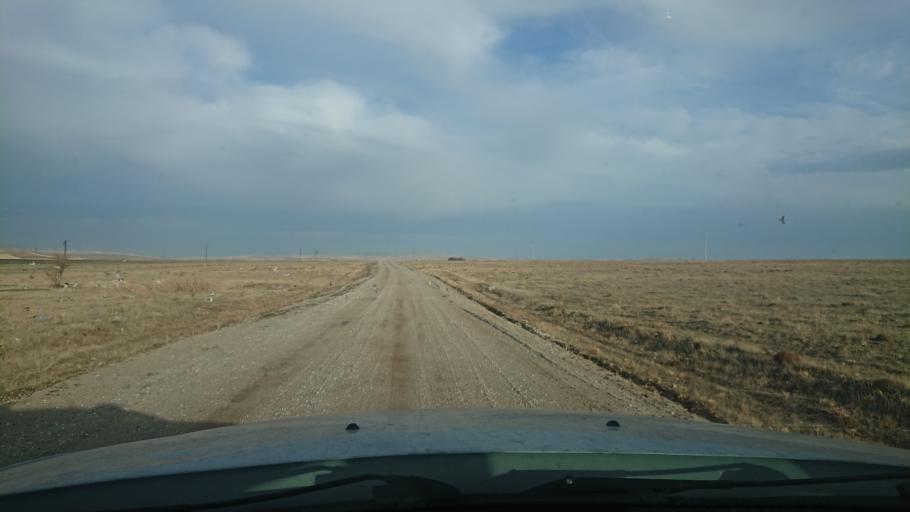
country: TR
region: Aksaray
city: Agacoren
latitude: 38.7166
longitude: 33.8687
